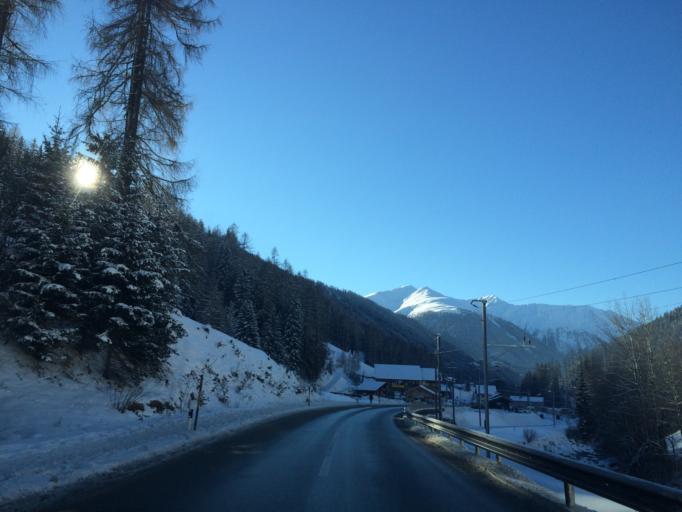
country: CH
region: Grisons
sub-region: Praettigau/Davos District
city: Davos
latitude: 46.7483
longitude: 9.7811
